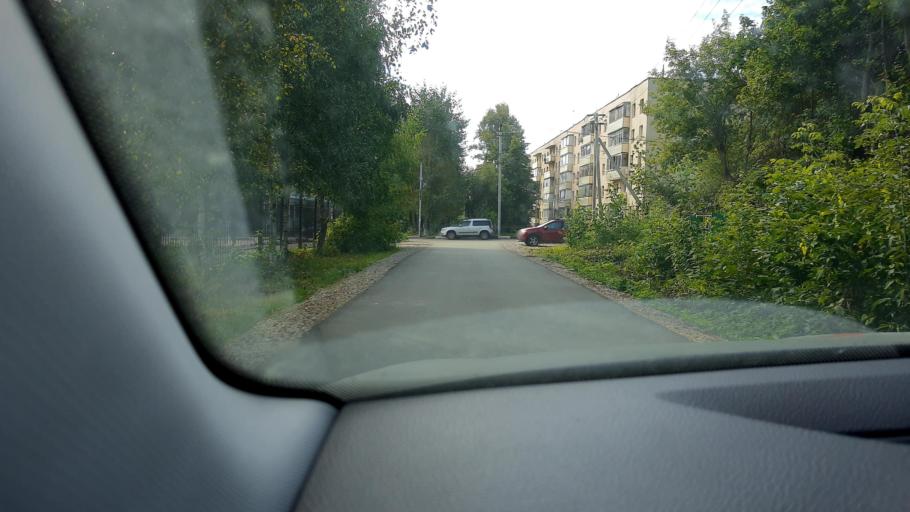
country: RU
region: Moskovskaya
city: Vidnoye
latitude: 55.5167
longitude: 37.6859
